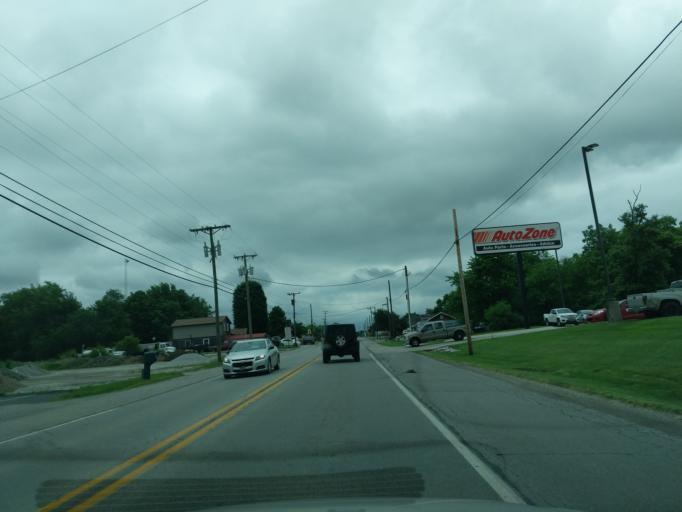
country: US
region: Indiana
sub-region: Madison County
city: Elwood
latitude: 40.2771
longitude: -85.8161
